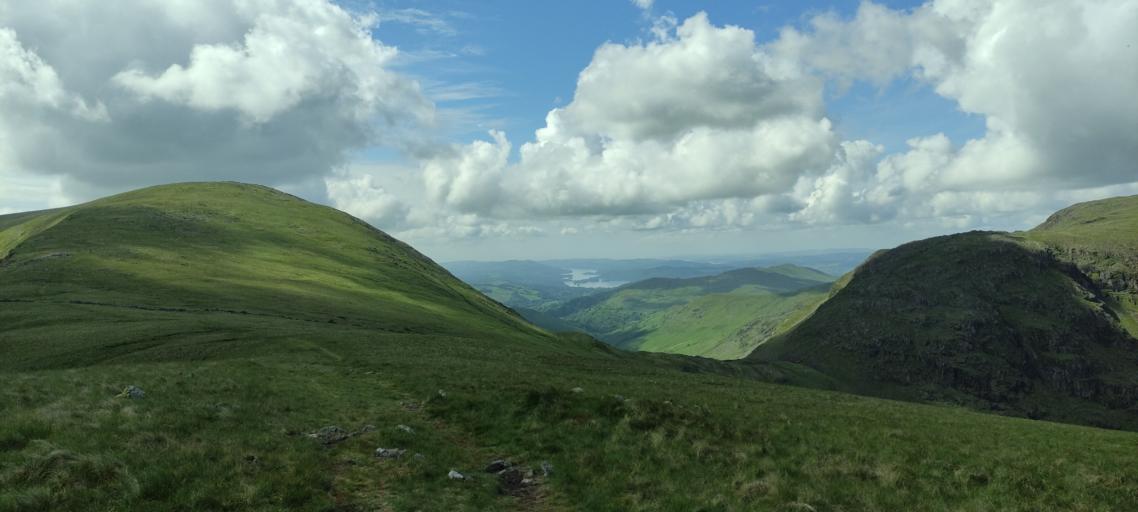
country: GB
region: England
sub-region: Cumbria
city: Ambleside
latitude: 54.4912
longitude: -2.8821
